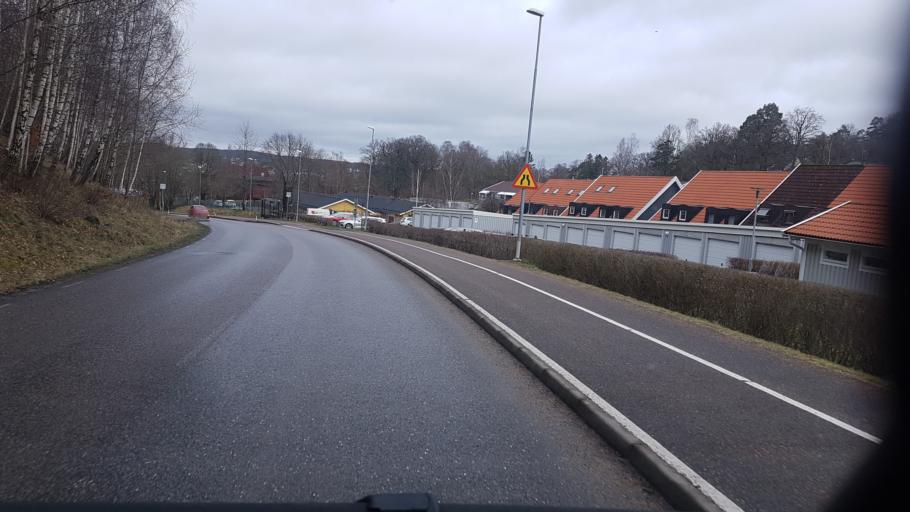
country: SE
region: Vaestra Goetaland
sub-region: Lerums Kommun
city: Lerum
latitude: 57.7542
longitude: 12.2580
